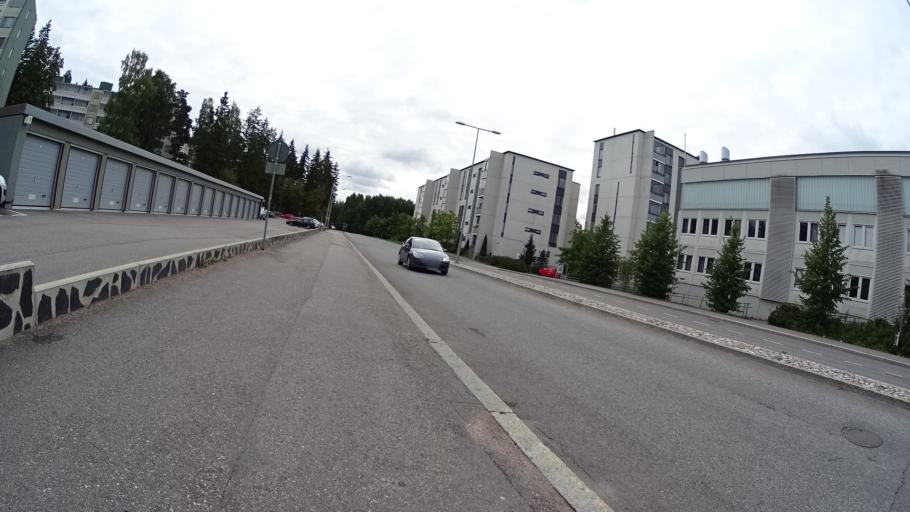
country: FI
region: Uusimaa
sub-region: Helsinki
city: Teekkarikylae
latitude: 60.2705
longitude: 24.8565
